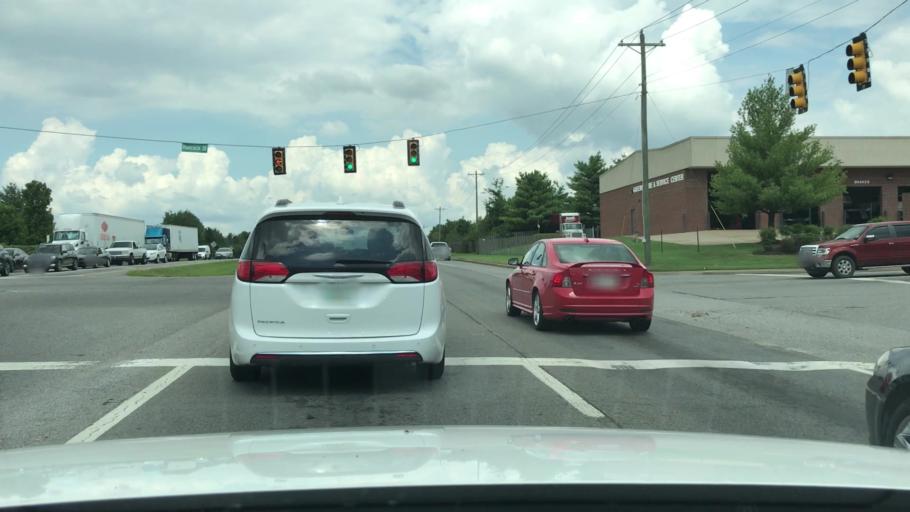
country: US
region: Tennessee
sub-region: Sumner County
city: Gallatin
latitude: 36.3723
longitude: -86.4630
